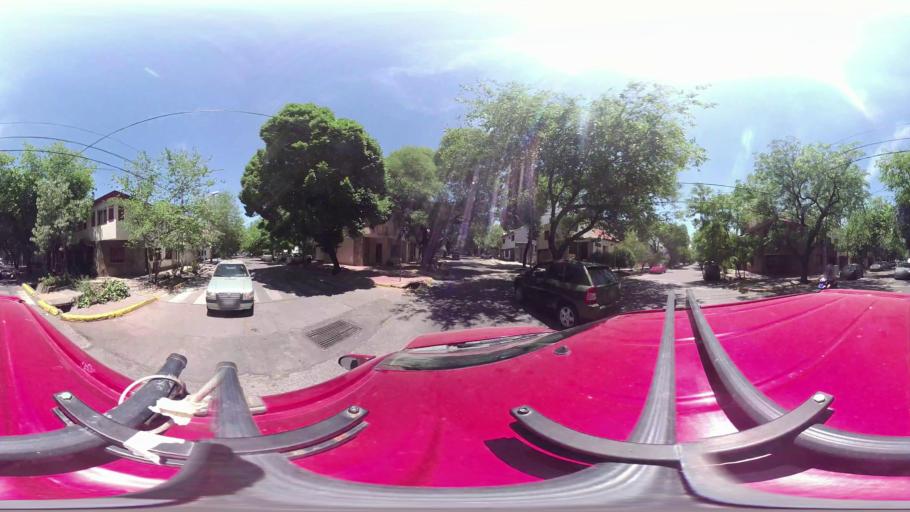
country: AR
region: Mendoza
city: Mendoza
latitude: -32.8994
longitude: -68.8528
